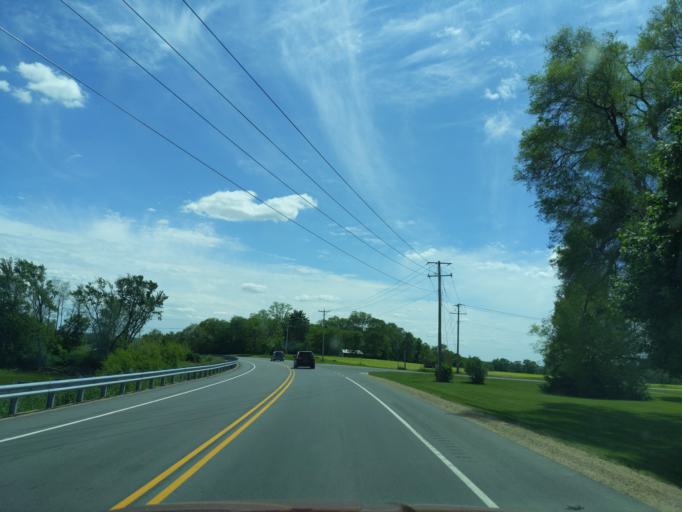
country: US
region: Wisconsin
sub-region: Columbia County
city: Pardeeville
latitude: 43.5106
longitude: -89.3066
